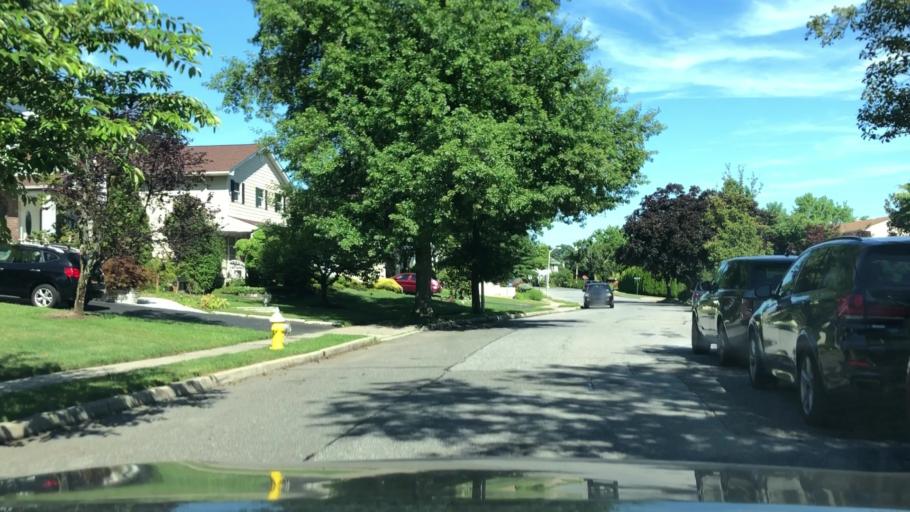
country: US
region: New York
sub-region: Nassau County
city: Manhasset Hills
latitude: 40.7629
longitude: -73.6872
